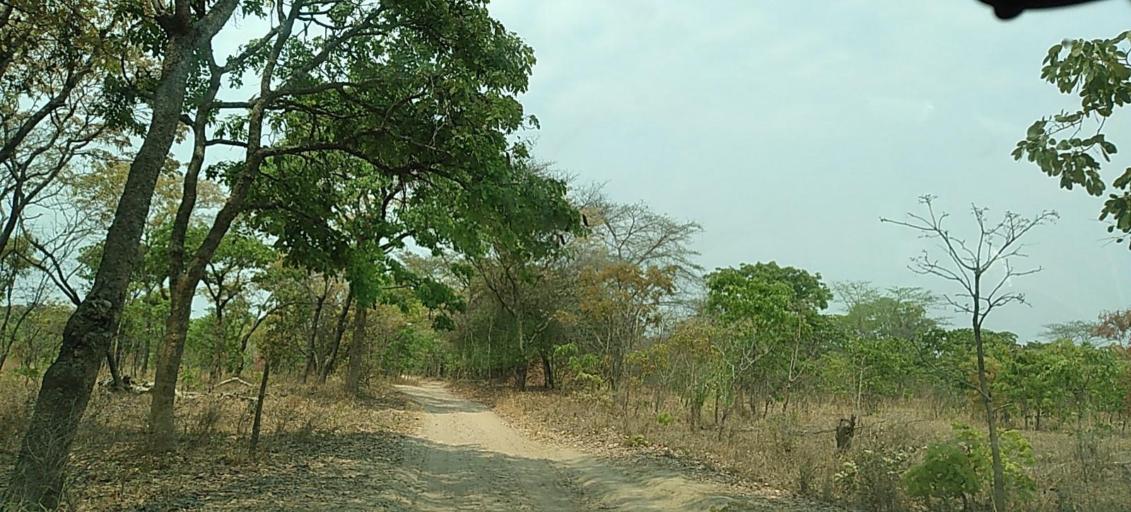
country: ZM
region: North-Western
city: Kabompo
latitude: -13.5507
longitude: 24.4497
